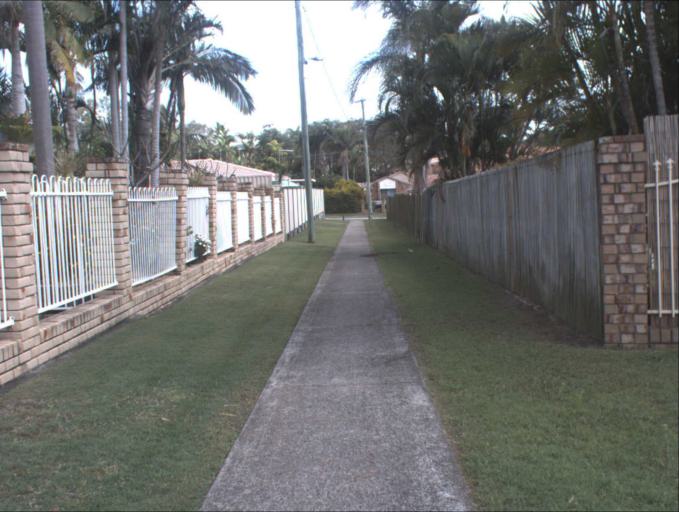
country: AU
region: Queensland
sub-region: Logan
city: Park Ridge South
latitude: -27.6771
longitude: 153.0348
